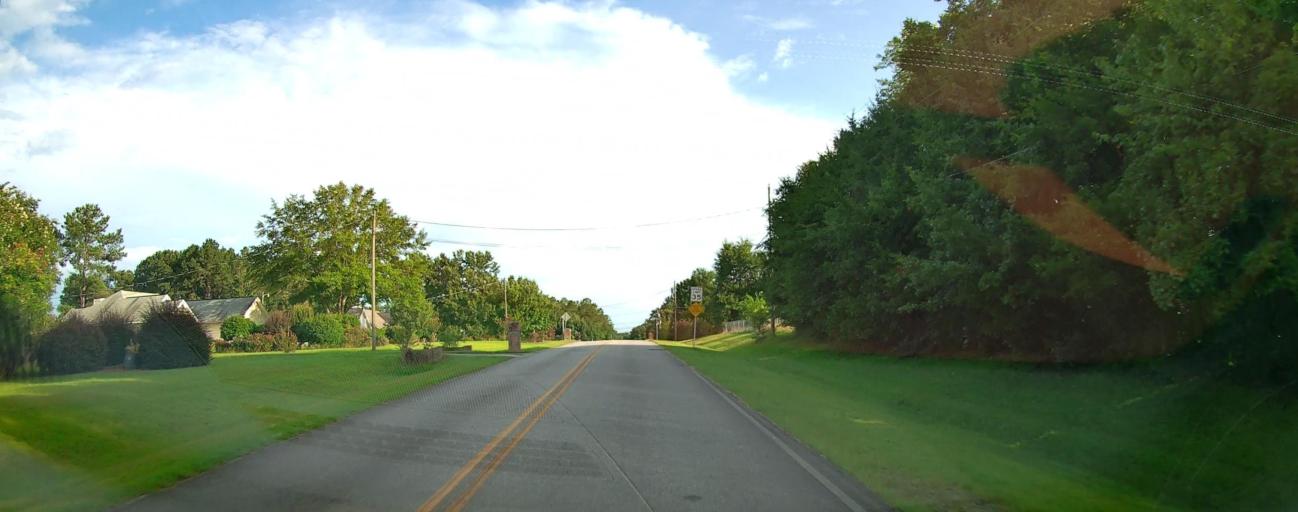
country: US
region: Georgia
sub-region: Peach County
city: Byron
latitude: 32.7281
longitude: -83.7467
